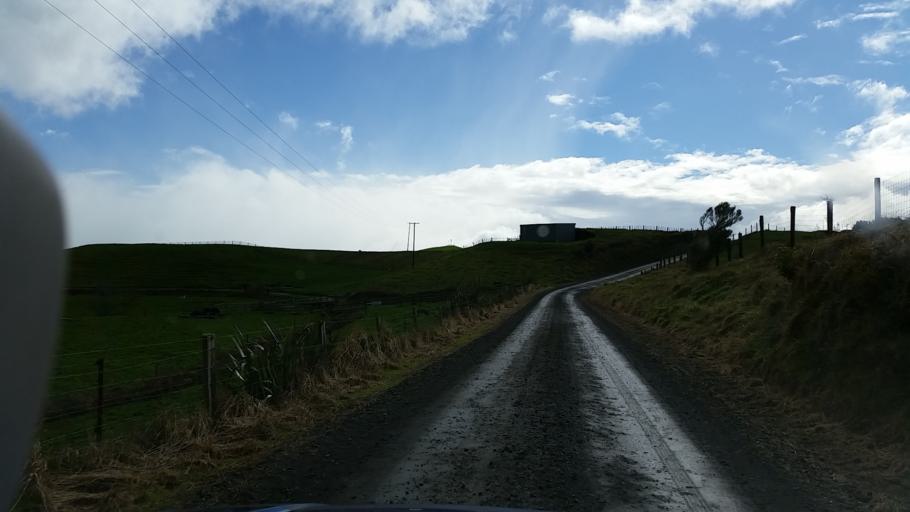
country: NZ
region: Taranaki
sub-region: South Taranaki District
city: Eltham
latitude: -39.2824
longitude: 174.3083
